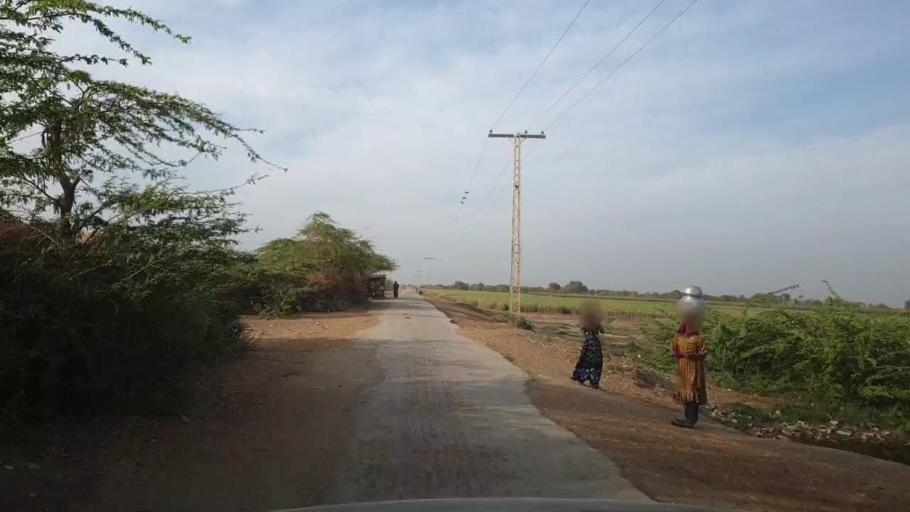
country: PK
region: Sindh
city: Kunri
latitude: 25.1963
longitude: 69.5199
